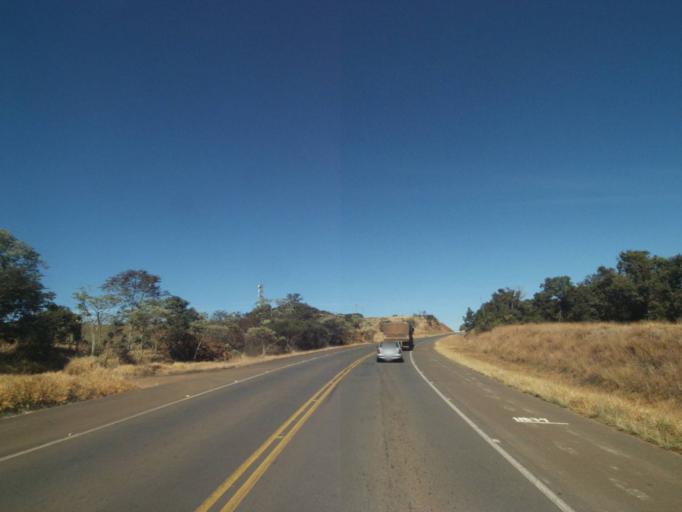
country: BR
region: Parana
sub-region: Tibagi
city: Tibagi
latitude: -24.7226
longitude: -50.4505
